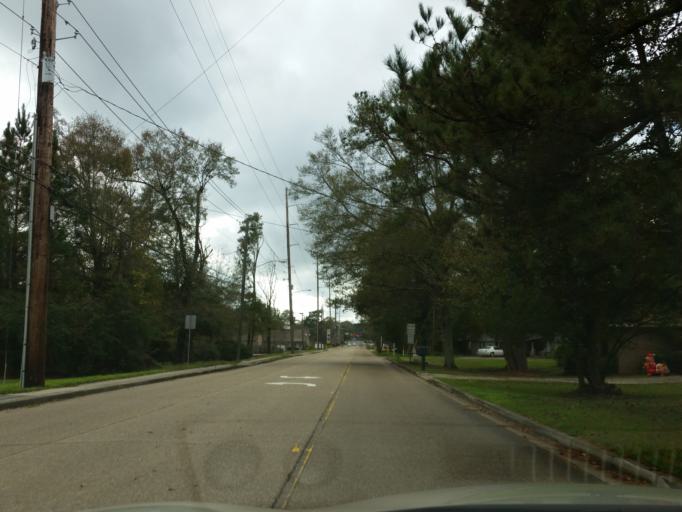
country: US
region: Mississippi
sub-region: Forrest County
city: Hattiesburg
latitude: 31.3078
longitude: -89.3312
